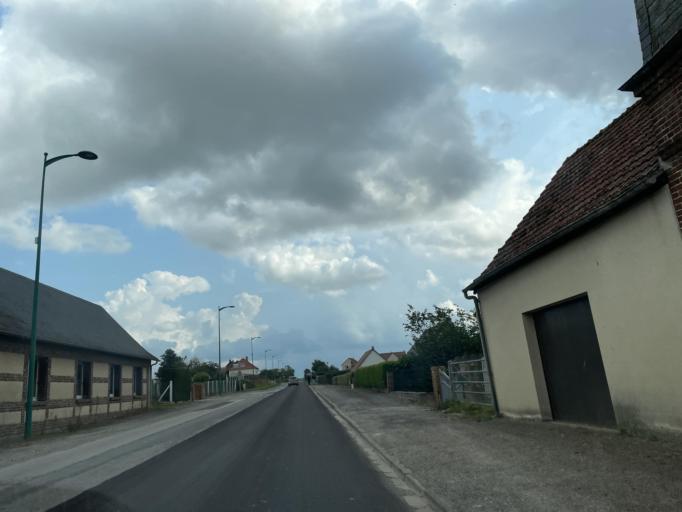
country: FR
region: Haute-Normandie
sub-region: Departement de la Seine-Maritime
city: Envermeu
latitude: 49.8696
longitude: 1.3243
